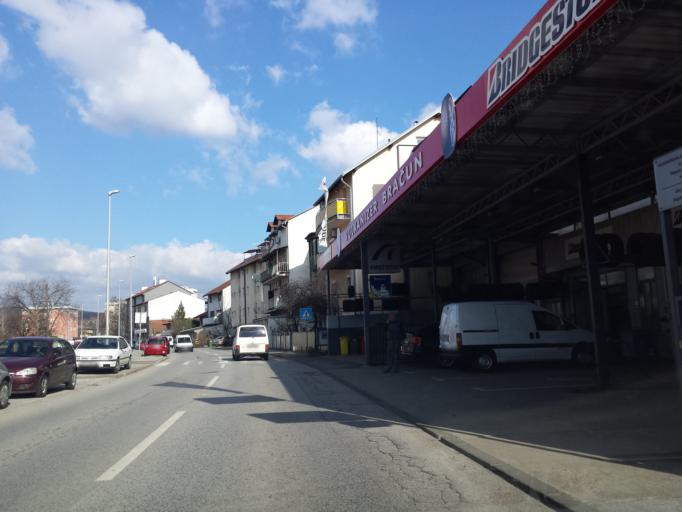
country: HR
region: Grad Zagreb
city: Jankomir
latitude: 45.7965
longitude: 15.9315
